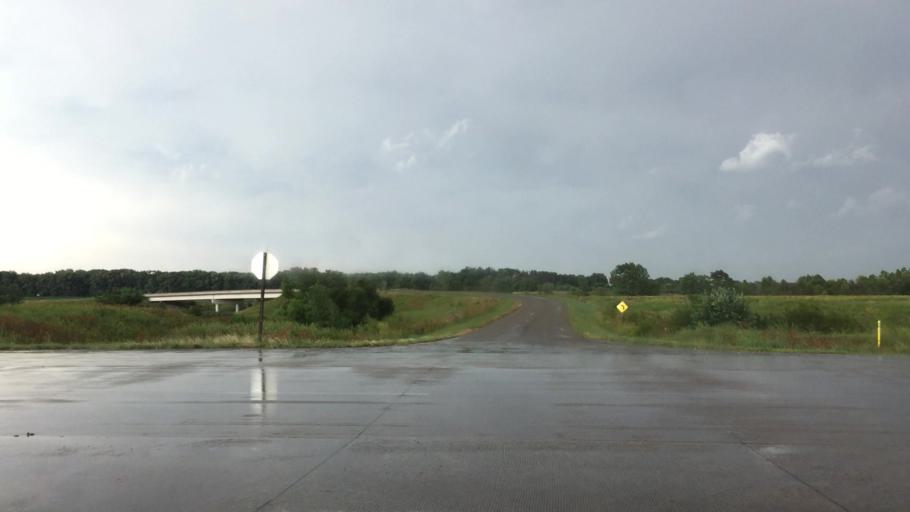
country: US
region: Iowa
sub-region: Henry County
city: Mount Pleasant
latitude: 40.9906
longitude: -91.5444
